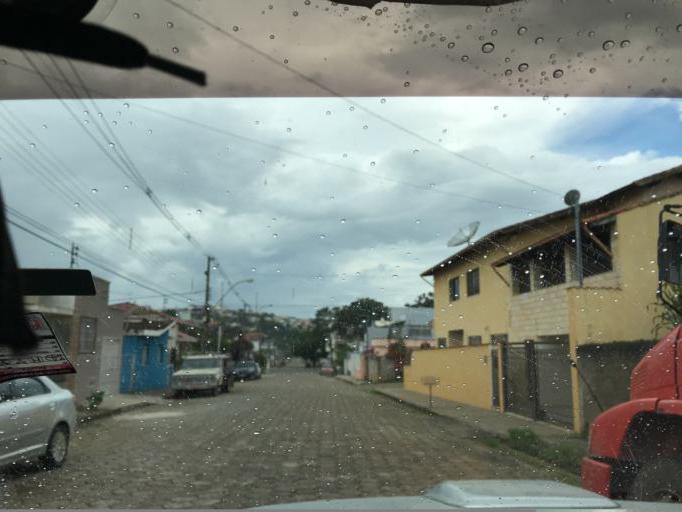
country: BR
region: Minas Gerais
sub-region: Tres Coracoes
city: Tres Coracoes
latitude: -21.7045
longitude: -45.2517
